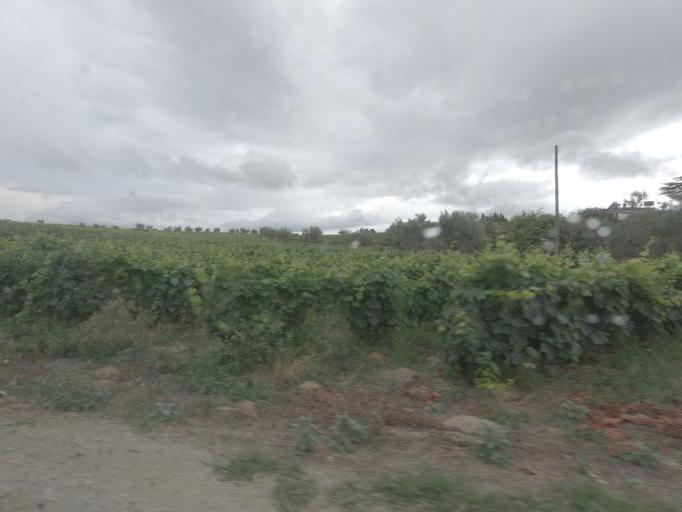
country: PT
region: Vila Real
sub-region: Sabrosa
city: Sabrosa
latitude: 41.2526
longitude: -7.5008
